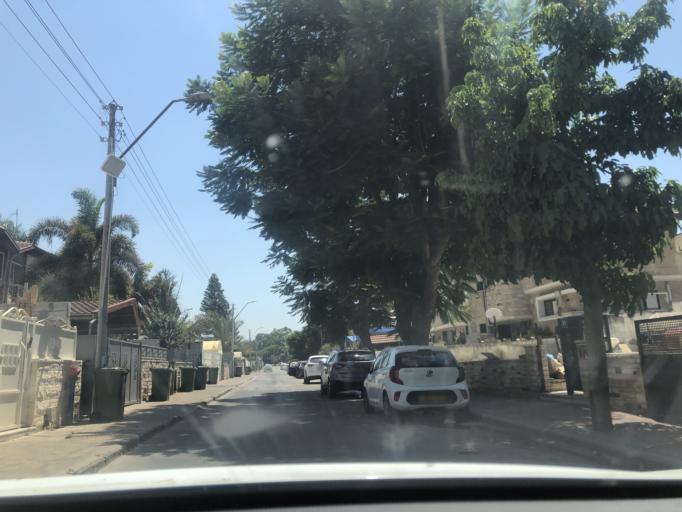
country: IL
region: Central District
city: Lod
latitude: 31.9384
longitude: 34.8897
